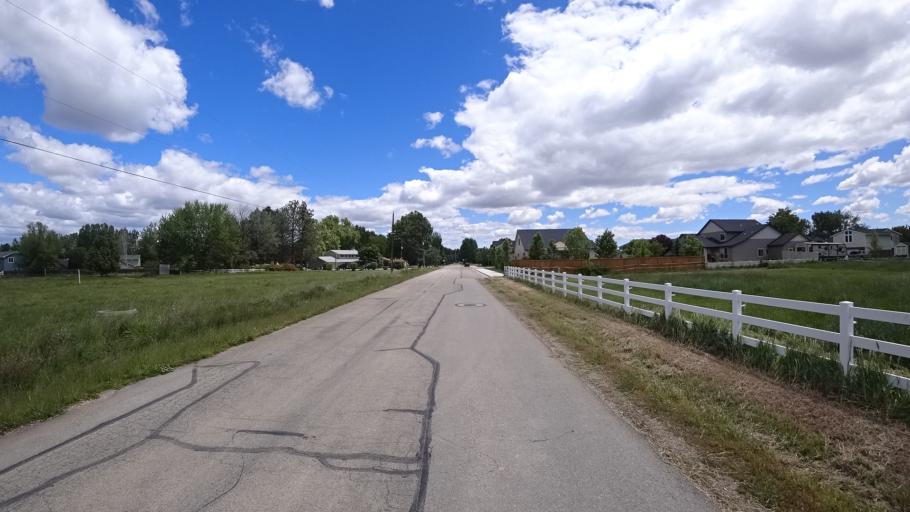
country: US
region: Idaho
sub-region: Ada County
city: Eagle
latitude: 43.6448
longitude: -116.3409
